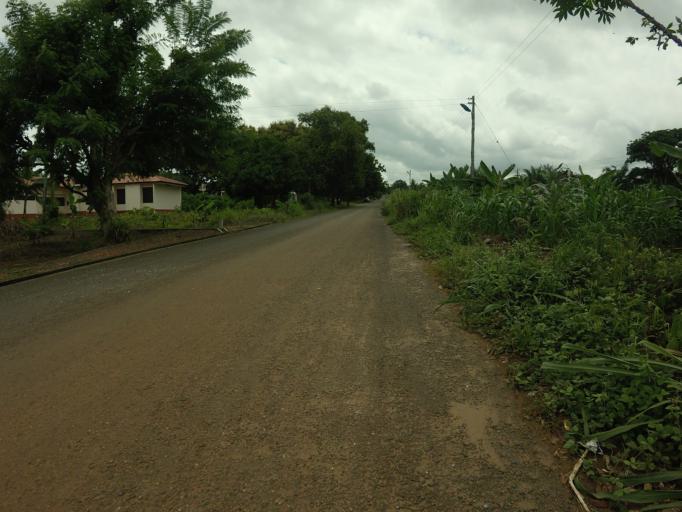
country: GH
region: Volta
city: Ho
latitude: 6.5954
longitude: 0.4593
